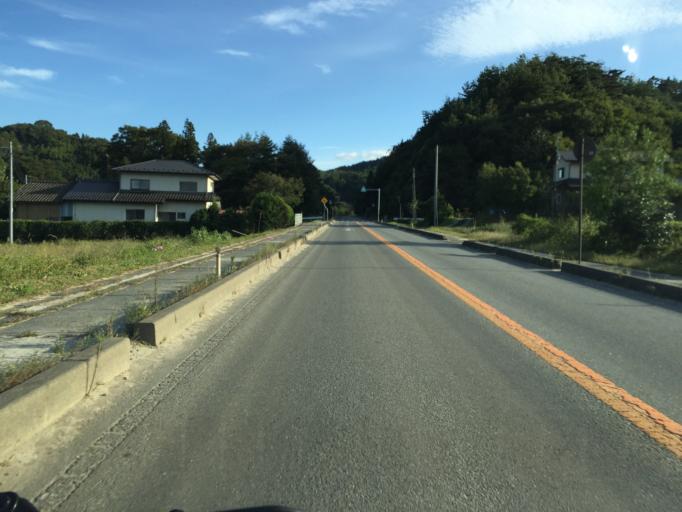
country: JP
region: Fukushima
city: Hobaramachi
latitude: 37.6962
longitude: 140.6082
